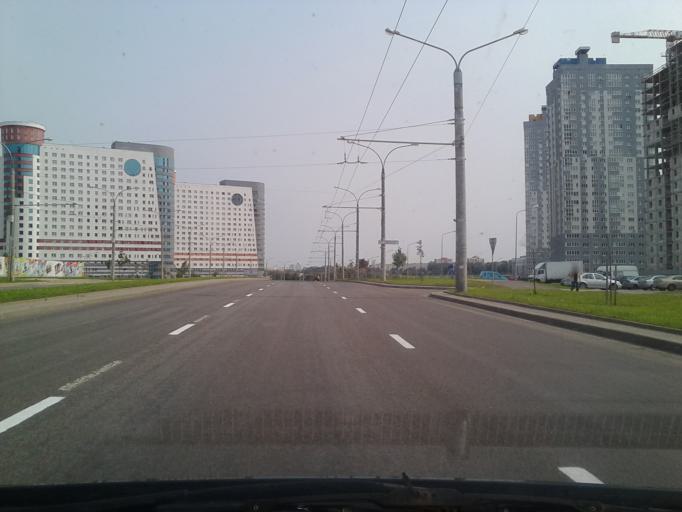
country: BY
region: Minsk
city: Novoye Medvezhino
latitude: 53.8561
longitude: 27.4797
